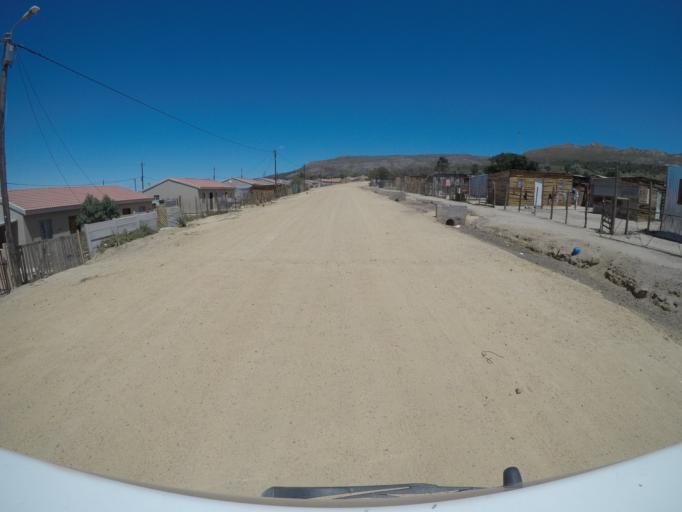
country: ZA
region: Western Cape
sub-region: Overberg District Municipality
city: Grabouw
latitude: -34.2222
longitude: 19.1936
